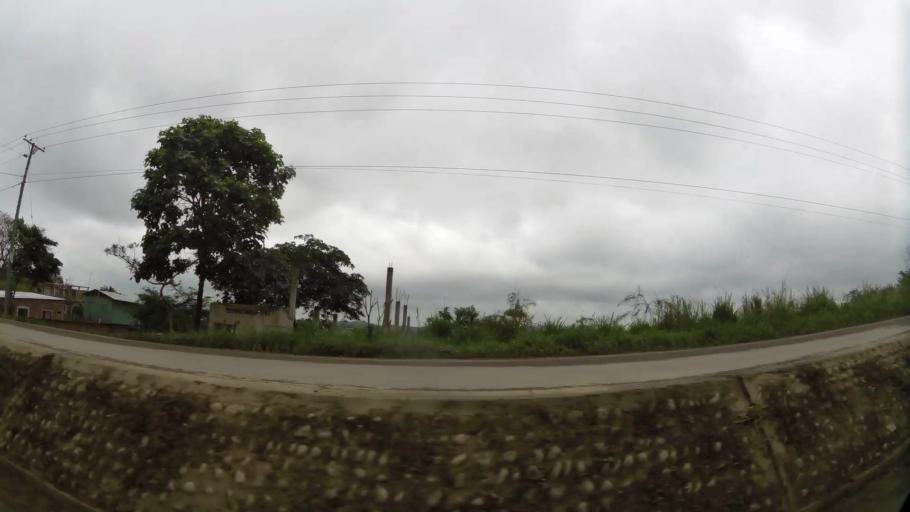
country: EC
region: El Oro
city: Pasaje
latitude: -3.3300
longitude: -79.7820
